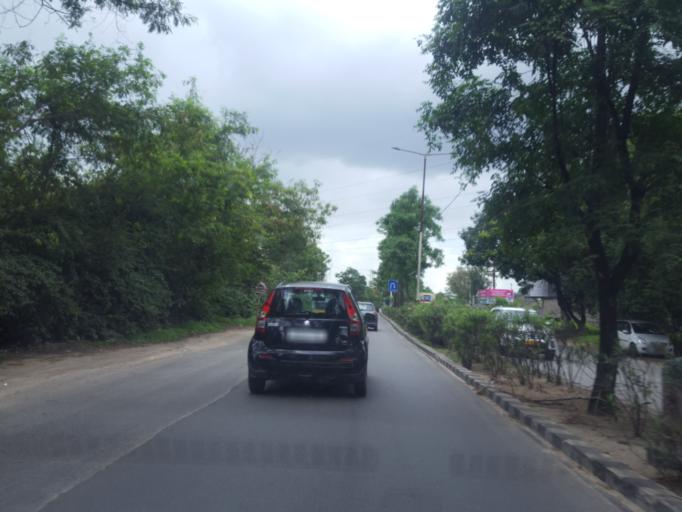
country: IN
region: Telangana
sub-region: Medak
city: Serilingampalle
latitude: 17.4561
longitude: 78.3405
